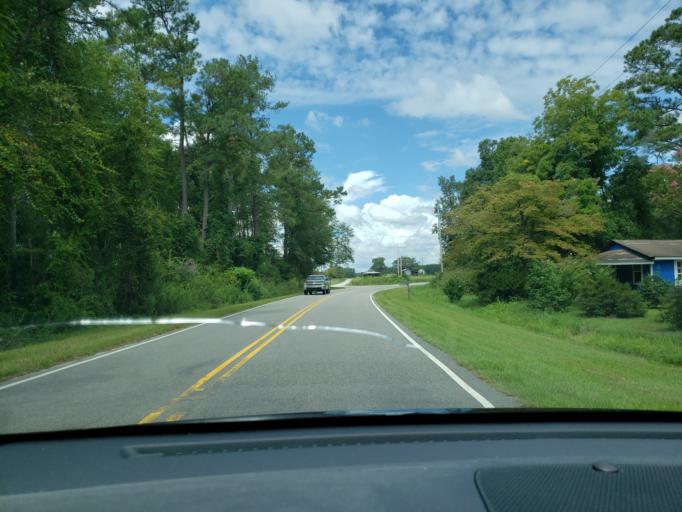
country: US
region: North Carolina
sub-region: Columbus County
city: Tabor City
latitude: 34.1777
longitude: -78.7867
